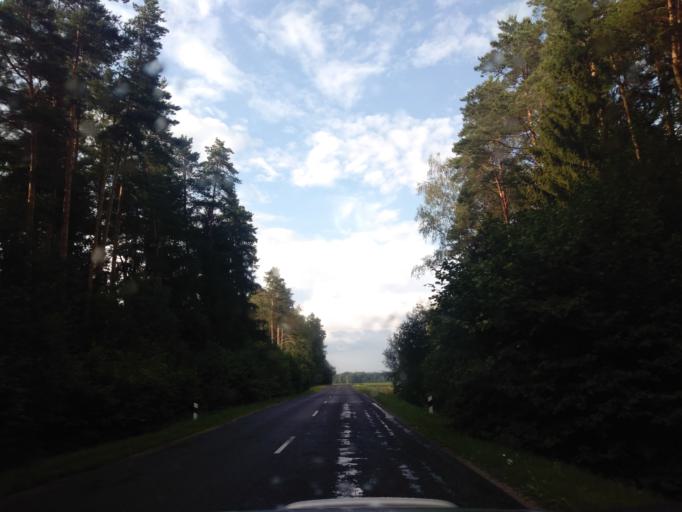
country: BY
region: Minsk
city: Kapyl'
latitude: 53.2759
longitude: 27.0777
